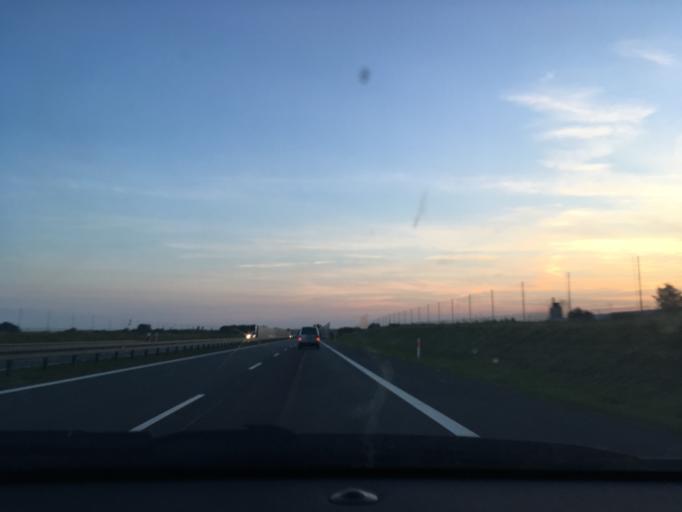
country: PL
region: Podlasie
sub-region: Powiat zambrowski
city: Zambrow
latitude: 52.9952
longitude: 22.2373
